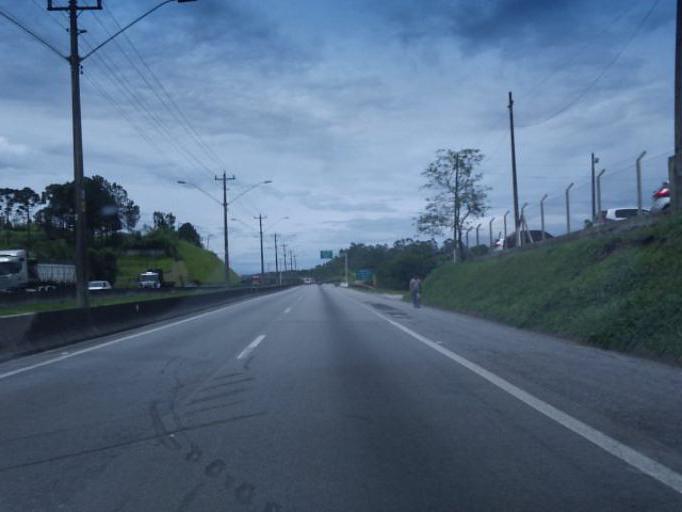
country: BR
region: Sao Paulo
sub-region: Itapecerica Da Serra
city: Itapecerica da Serra
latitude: -23.7005
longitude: -46.8688
